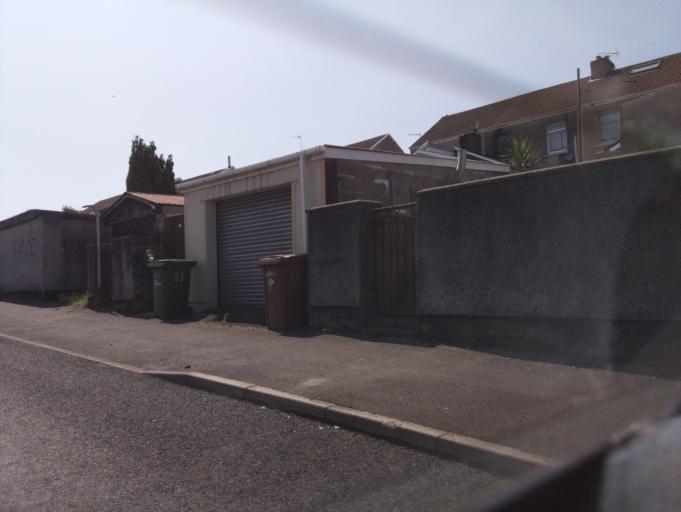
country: GB
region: Wales
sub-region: Caerphilly County Borough
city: Pengam
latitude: 51.6691
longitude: -3.2278
